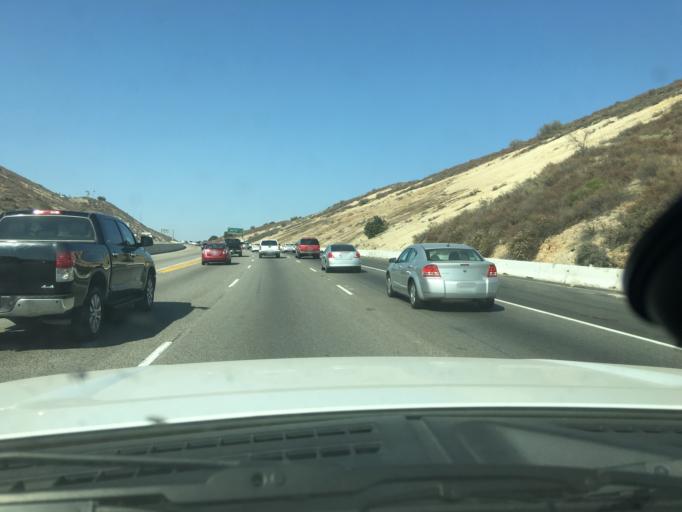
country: US
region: California
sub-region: Los Angeles County
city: Santa Clarita
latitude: 34.3854
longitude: -118.4832
